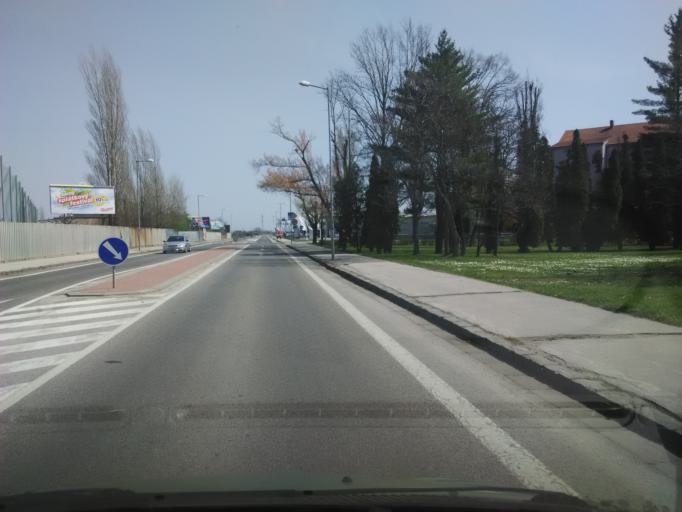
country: SK
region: Trnavsky
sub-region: Okres Galanta
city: Galanta
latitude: 48.1934
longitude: 17.7399
